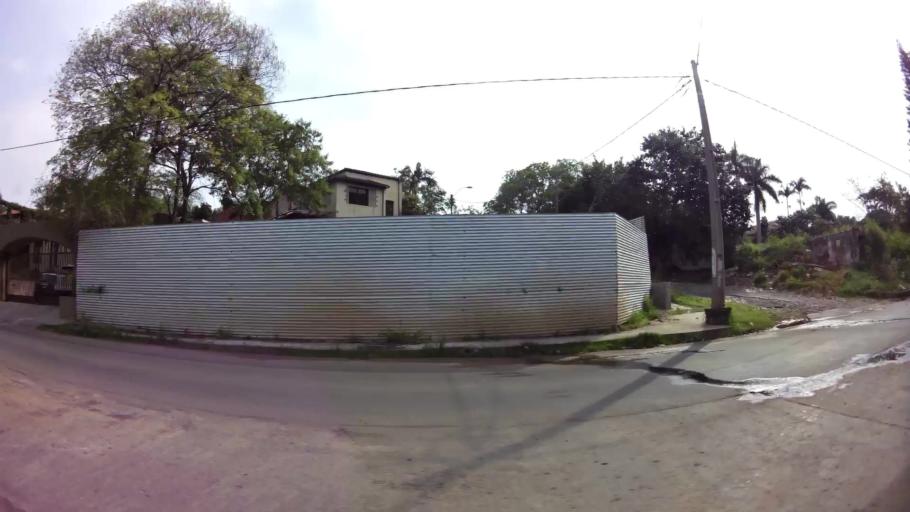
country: PY
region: Asuncion
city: Asuncion
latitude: -25.2666
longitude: -57.5755
